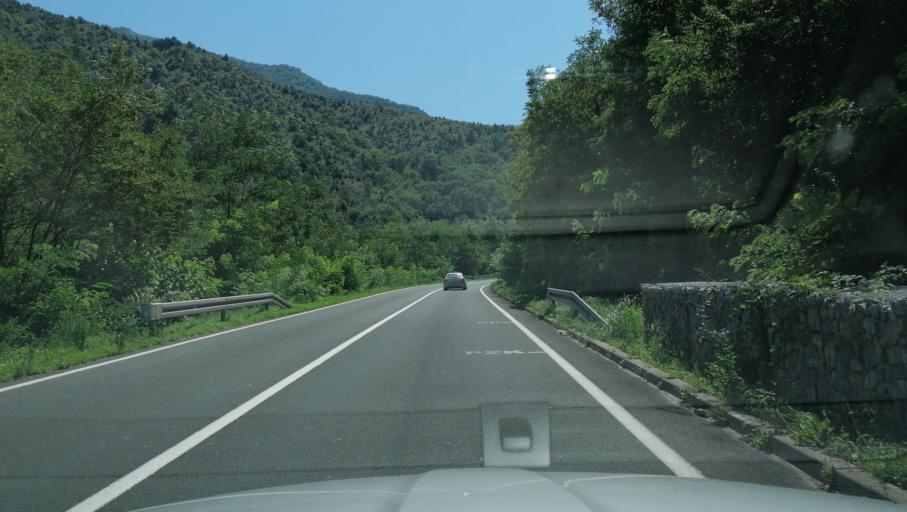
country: RS
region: Central Serbia
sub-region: Raski Okrug
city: Kraljevo
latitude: 43.6188
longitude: 20.5538
